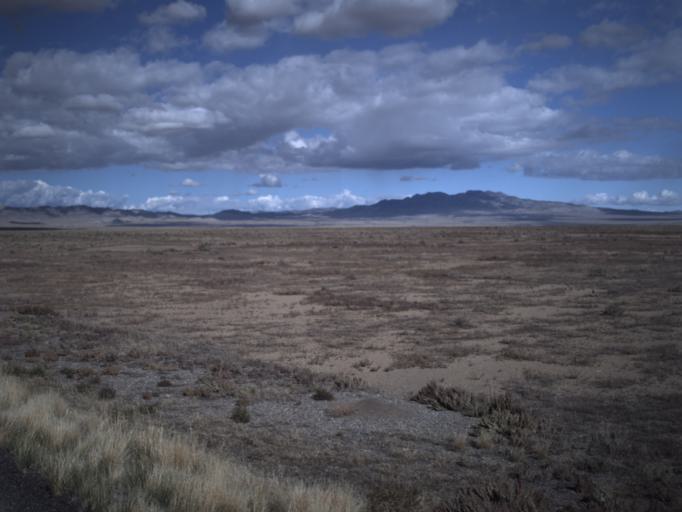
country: US
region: Utah
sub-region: Beaver County
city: Milford
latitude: 38.5256
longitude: -113.6638
